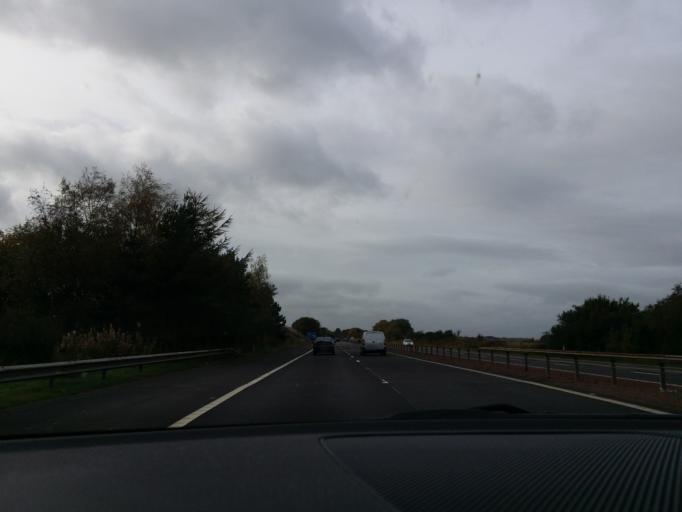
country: GB
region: Scotland
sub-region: West Lothian
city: Linlithgow
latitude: 55.9849
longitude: -3.6445
